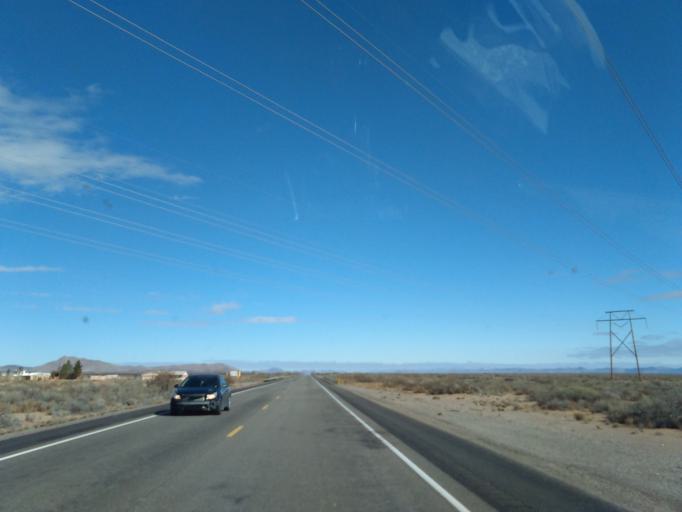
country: US
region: New Mexico
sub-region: Luna County
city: Deming
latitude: 32.3145
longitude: -107.6858
